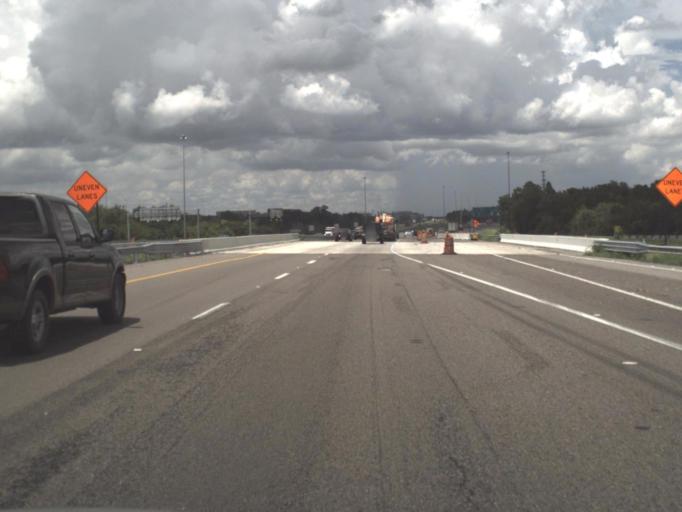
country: US
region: Florida
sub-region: Hillsborough County
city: Temple Terrace
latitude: 28.0551
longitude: -82.3536
